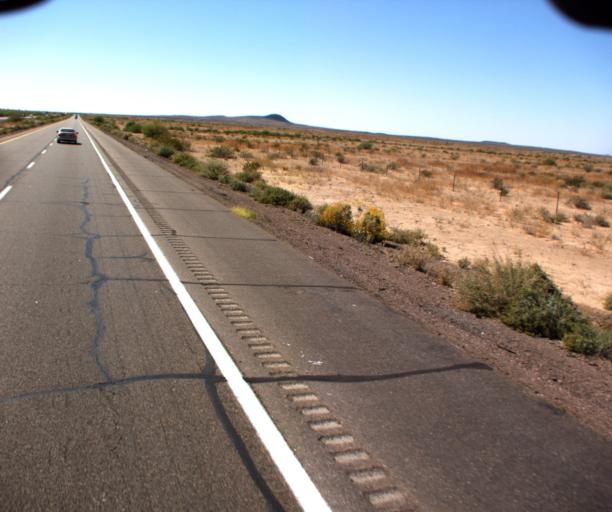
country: US
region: Arizona
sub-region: Maricopa County
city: Gila Bend
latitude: 32.8842
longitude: -113.0910
